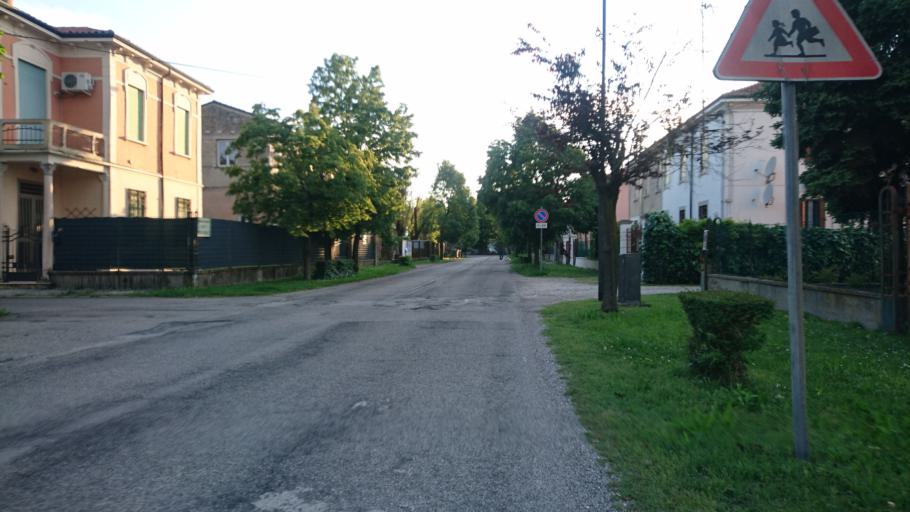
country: IT
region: Veneto
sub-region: Provincia di Rovigo
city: Castelmassa
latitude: 45.0192
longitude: 11.3088
